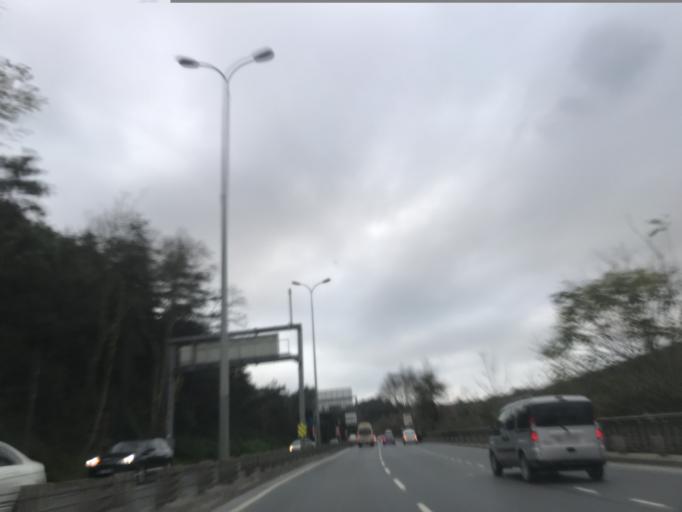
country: TR
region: Istanbul
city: Arikoey
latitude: 41.1504
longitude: 29.0297
